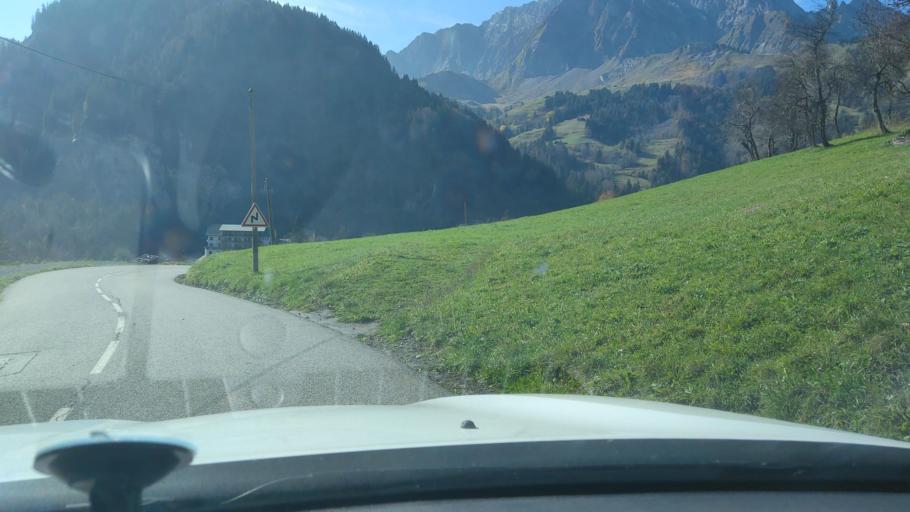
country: FR
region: Rhone-Alpes
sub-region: Departement de la Haute-Savoie
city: Praz-sur-Arly
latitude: 45.8669
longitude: 6.4981
